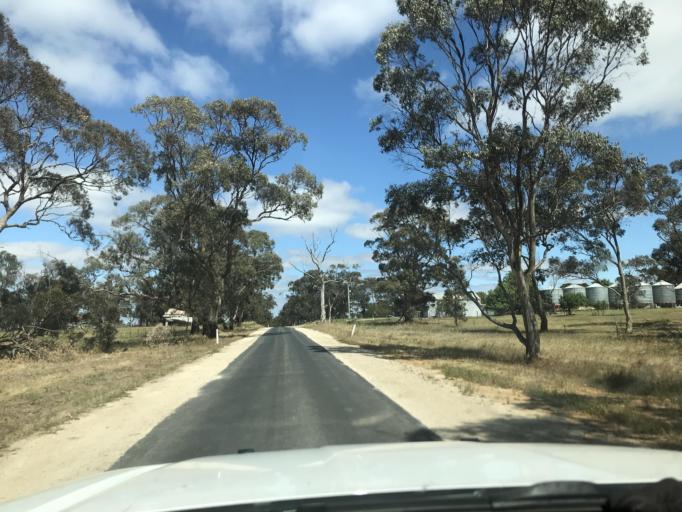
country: AU
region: South Australia
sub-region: Tatiara
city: Bordertown
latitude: -36.3062
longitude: 141.0757
